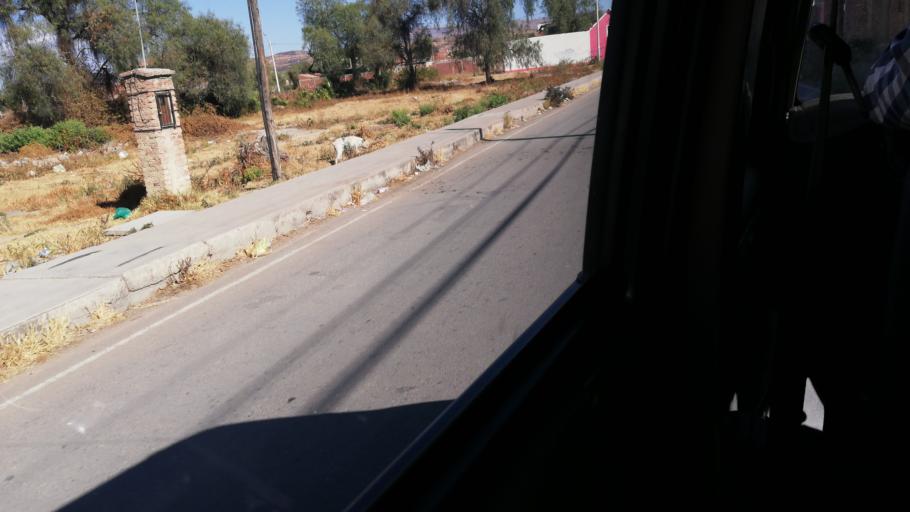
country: BO
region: Cochabamba
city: Cochabamba
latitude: -17.3938
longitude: -66.2530
